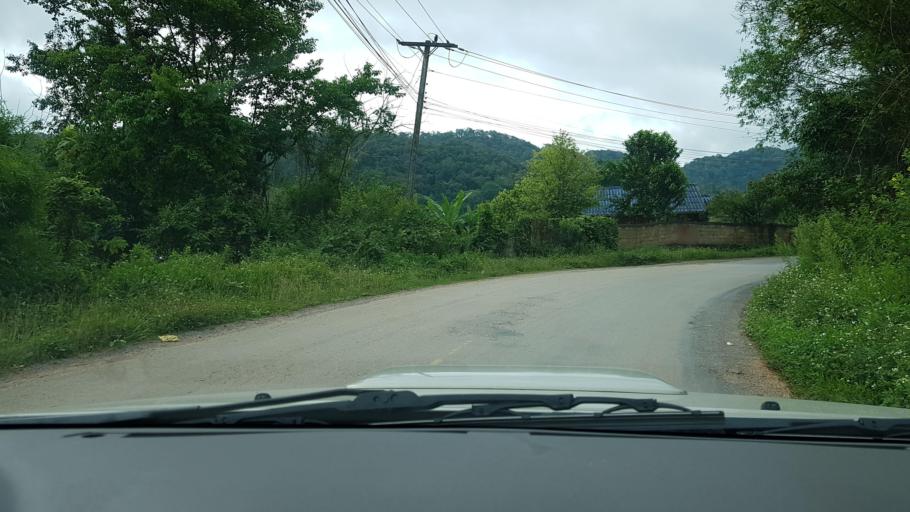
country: LA
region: Oudomxai
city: Muang Xay
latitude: 20.5774
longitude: 101.9227
